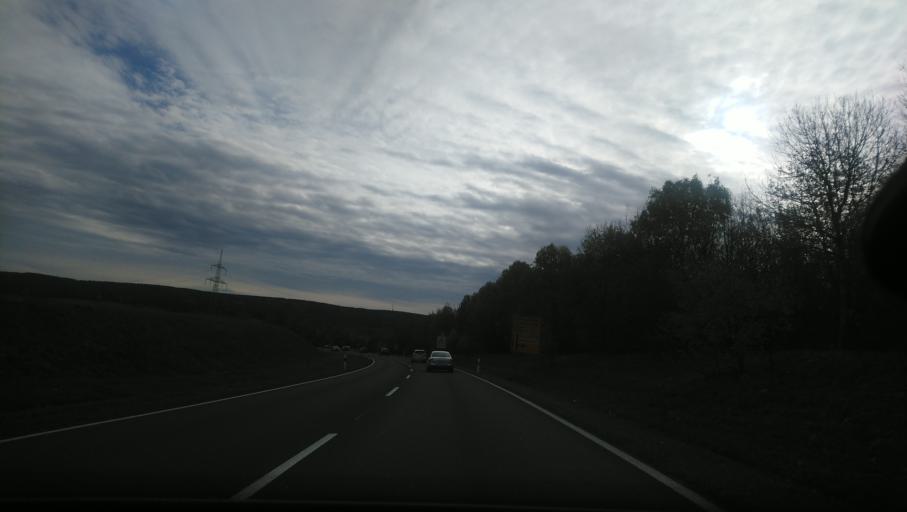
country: DE
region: Saxony
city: Zwonitz
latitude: 50.6532
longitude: 12.8117
